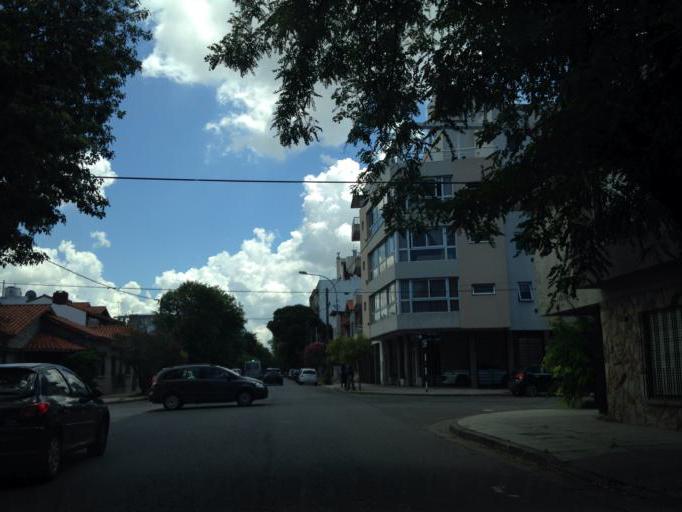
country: AR
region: Buenos Aires
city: Mar del Plata
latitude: -38.0128
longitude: -57.5517
